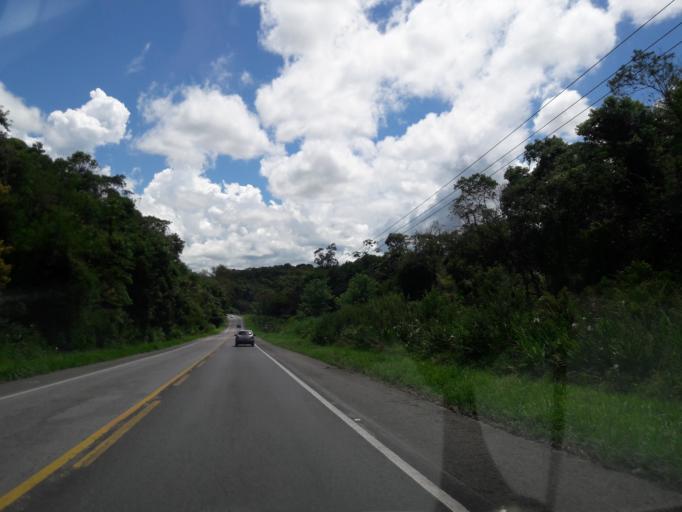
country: BR
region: Parana
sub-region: Antonina
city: Antonina
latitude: -25.4424
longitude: -48.7902
